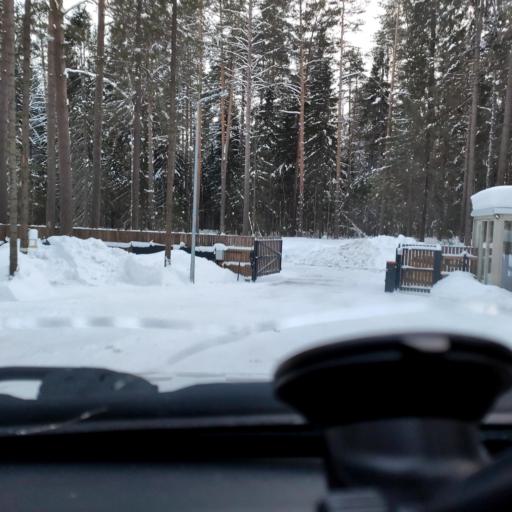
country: RU
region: Perm
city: Perm
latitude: 58.0733
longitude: 56.2611
